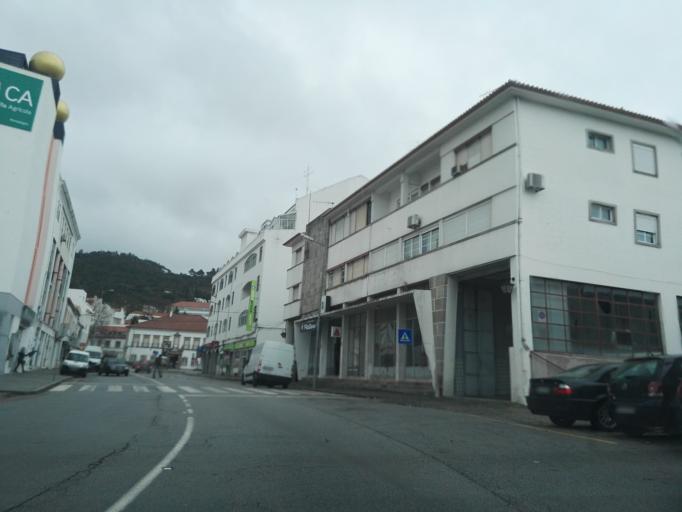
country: PT
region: Portalegre
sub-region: Portalegre
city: Portalegre
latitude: 39.2956
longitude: -7.4318
